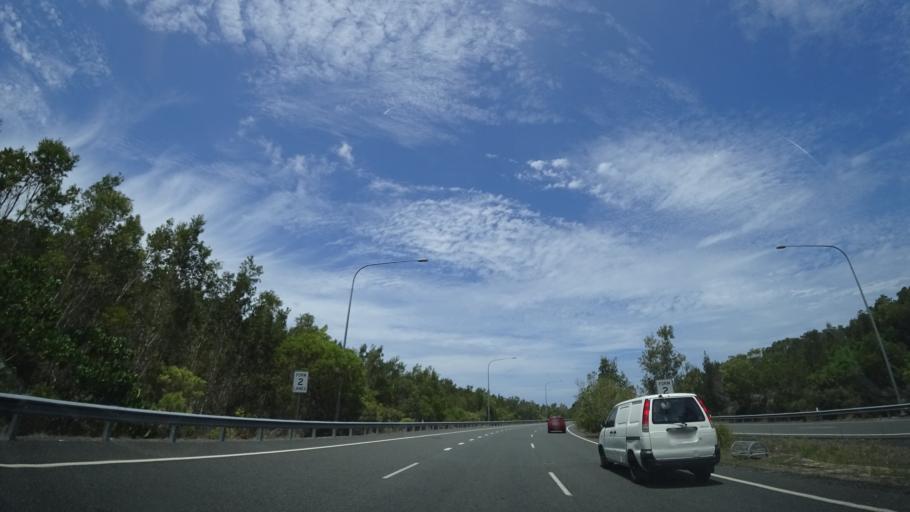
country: AU
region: Queensland
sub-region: Sunshine Coast
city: Buderim
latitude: -26.6102
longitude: 153.0802
